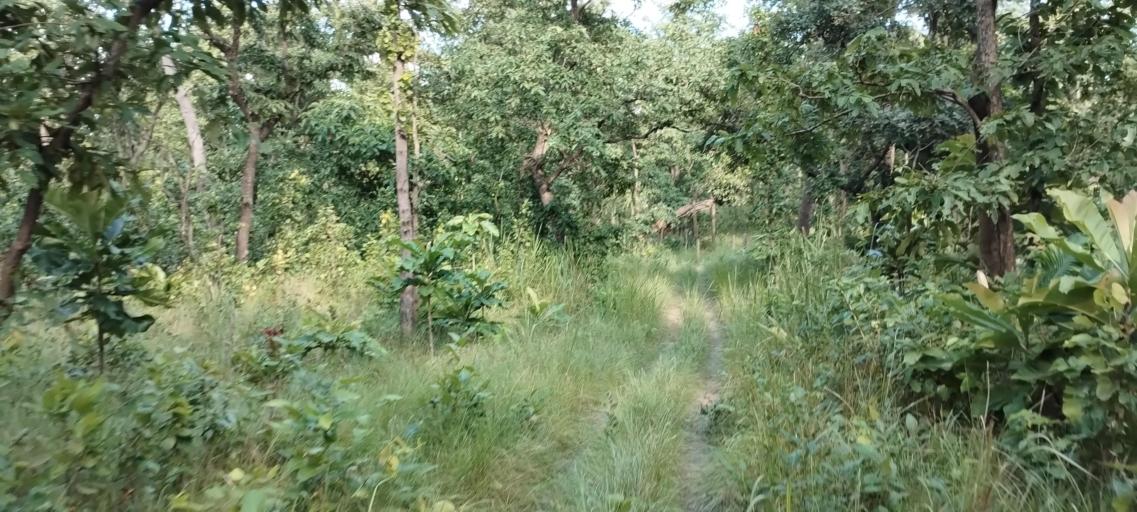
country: NP
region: Far Western
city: Tikapur
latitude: 28.5519
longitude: 81.2820
